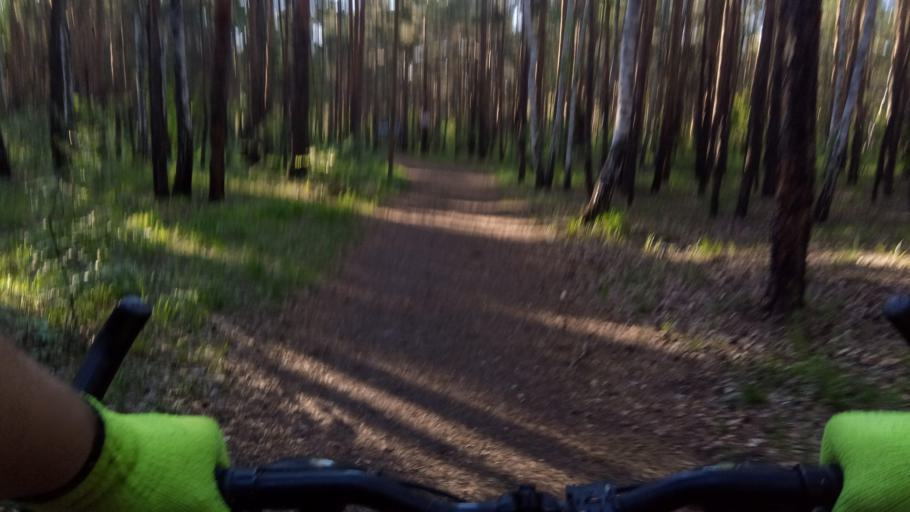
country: RU
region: Chelyabinsk
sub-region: Gorod Chelyabinsk
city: Chelyabinsk
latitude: 55.1288
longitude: 61.3397
